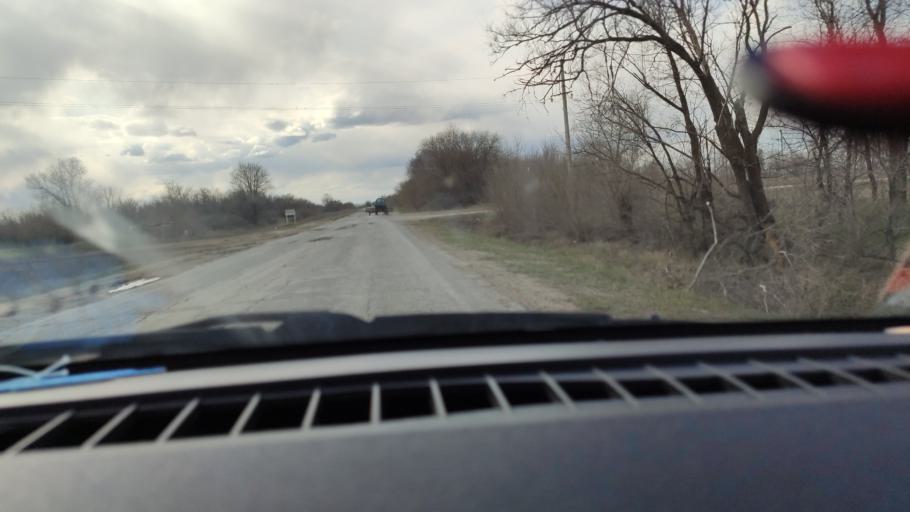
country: RU
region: Saratov
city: Rovnoye
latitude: 51.0424
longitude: 46.0643
